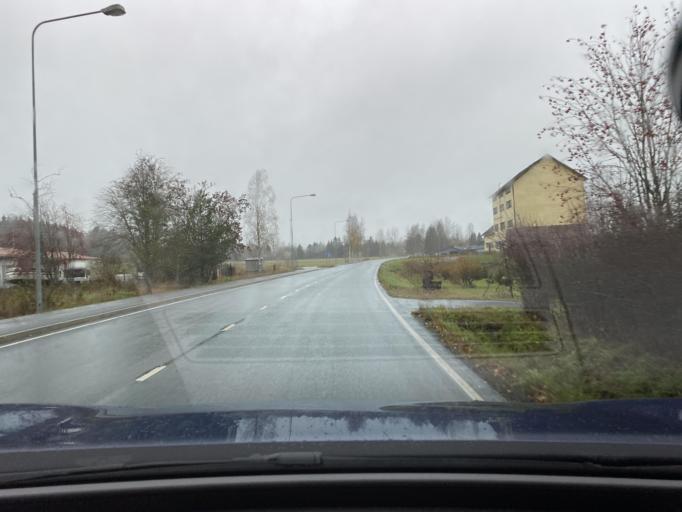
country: FI
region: Varsinais-Suomi
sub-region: Loimaa
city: Alastaro
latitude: 60.9423
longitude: 22.8684
